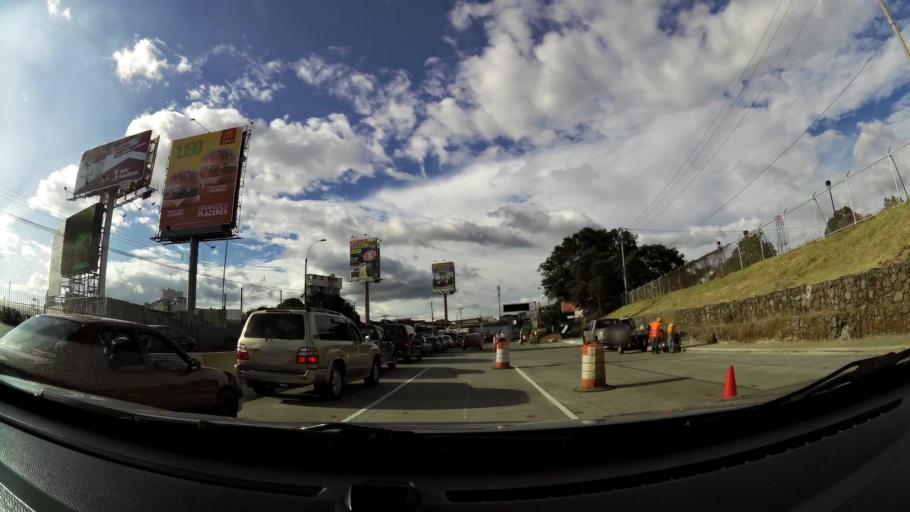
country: CR
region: Alajuela
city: Alajuela
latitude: 10.0080
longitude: -84.2125
